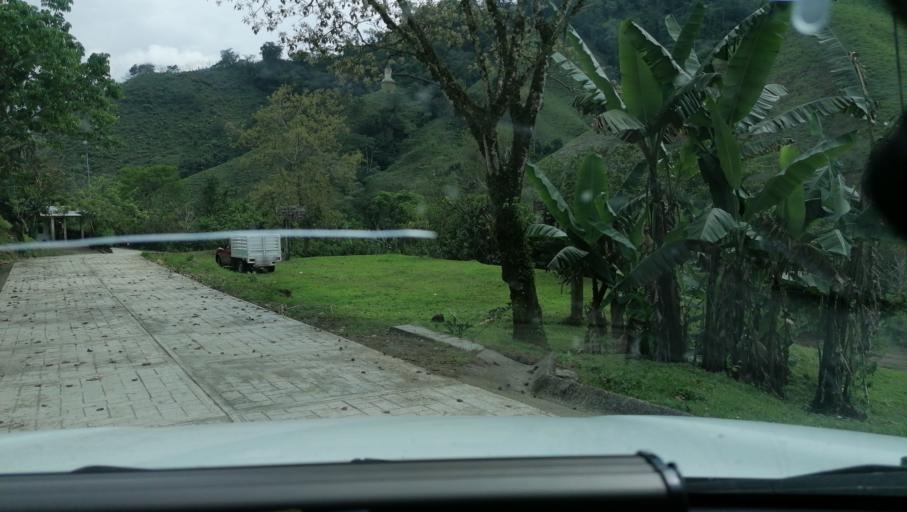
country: MX
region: Chiapas
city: Ocotepec
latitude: 17.3283
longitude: -93.1734
